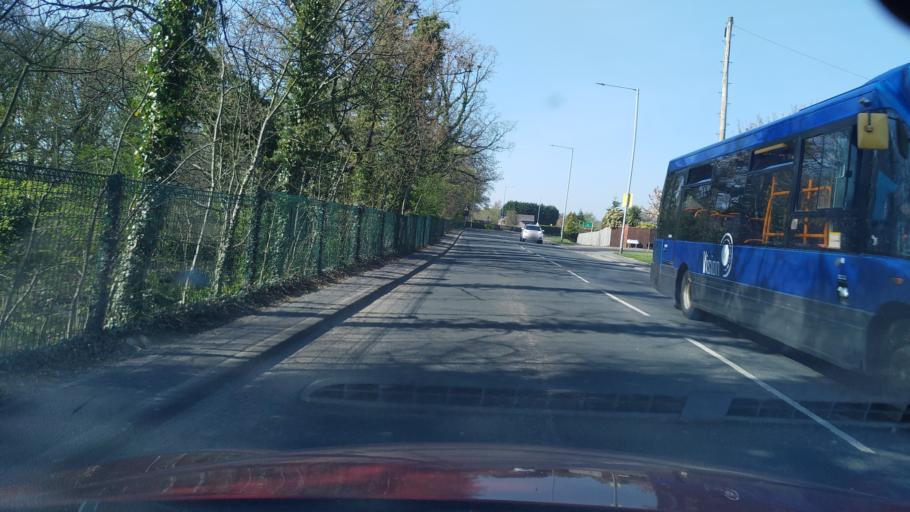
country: GB
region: England
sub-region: Lancashire
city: Adlington
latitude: 53.6204
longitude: -2.6113
